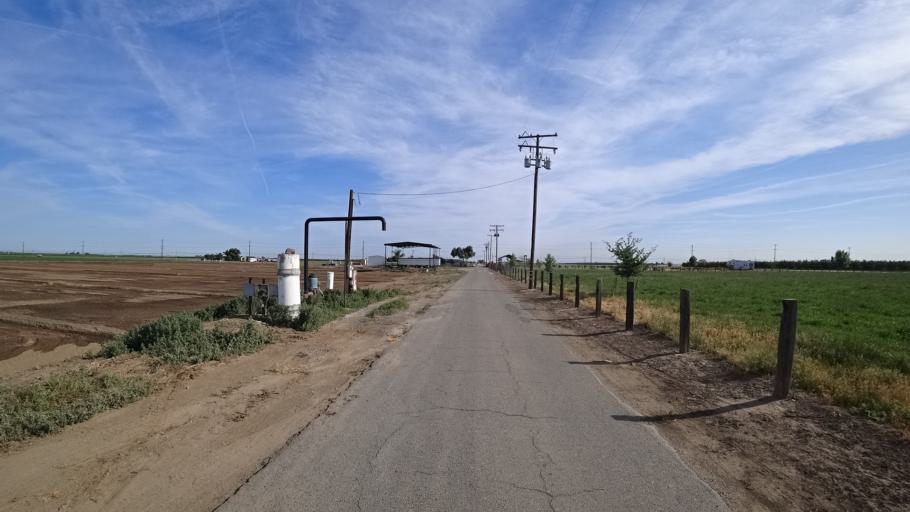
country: US
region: California
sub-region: Kings County
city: Home Garden
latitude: 36.3406
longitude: -119.5562
